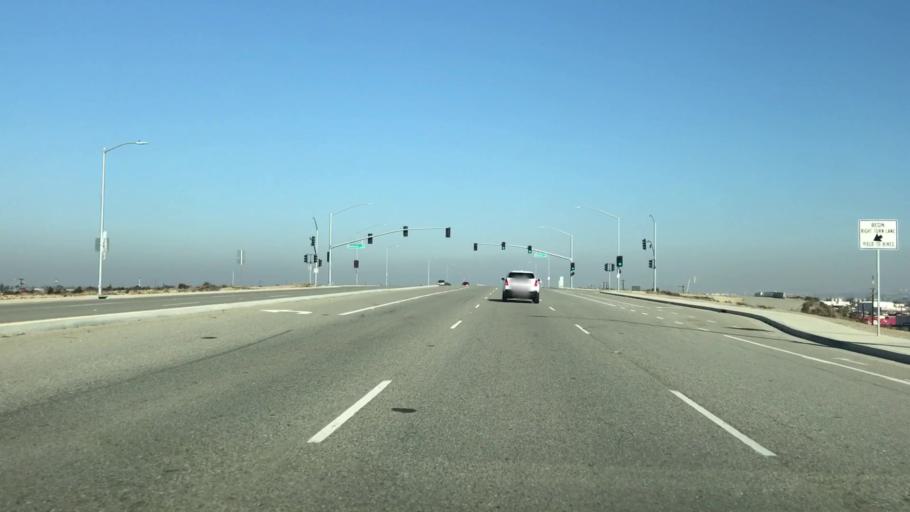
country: US
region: California
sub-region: Kern County
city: Greenacres
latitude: 35.3736
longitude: -119.0659
